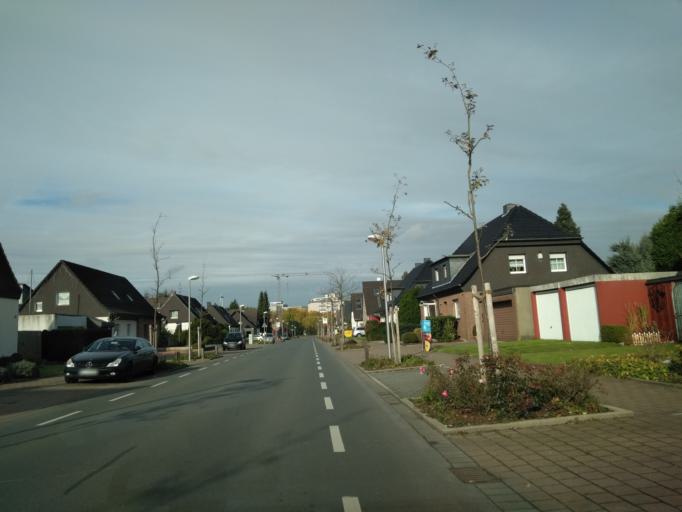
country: DE
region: North Rhine-Westphalia
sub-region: Regierungsbezirk Munster
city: Gladbeck
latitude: 51.5778
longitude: 6.9558
